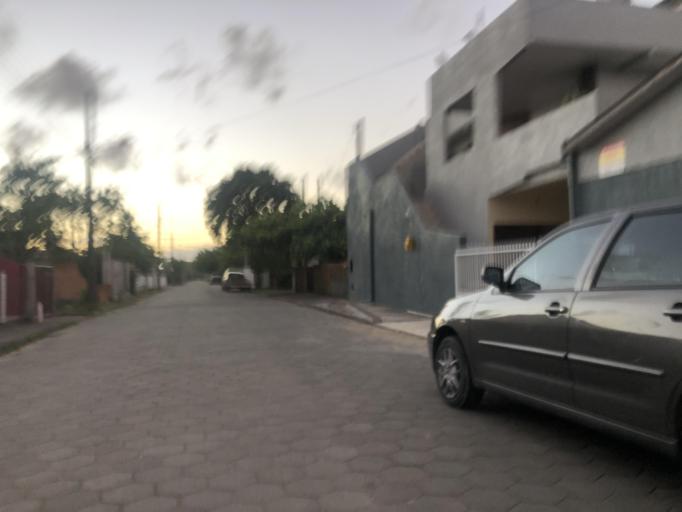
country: BR
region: Santa Catarina
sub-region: Sao Francisco Do Sul
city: Sao Francisco do Sul
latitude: -26.2204
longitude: -48.5317
